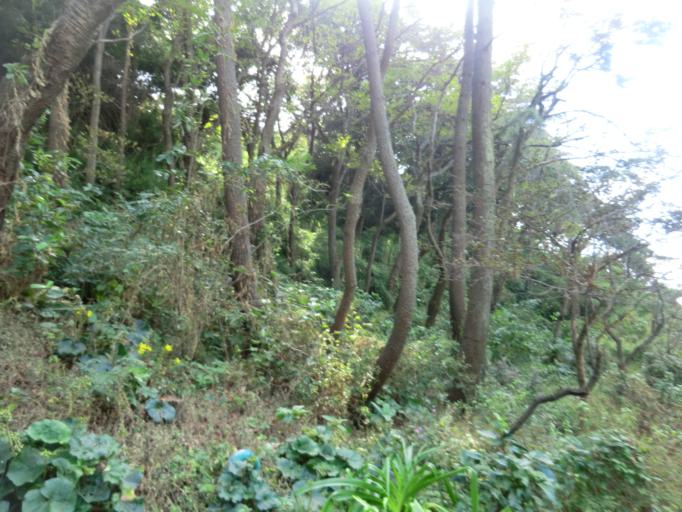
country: JP
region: Kanagawa
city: Yokohama
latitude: 35.4160
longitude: 139.6584
